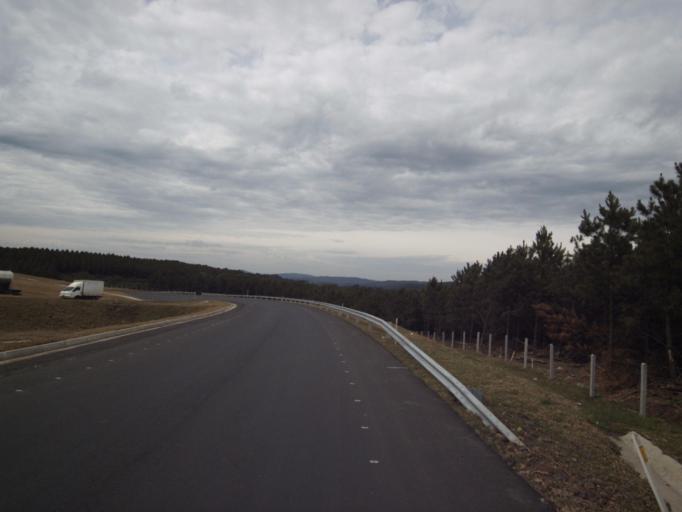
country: BR
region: Santa Catarina
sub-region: Cacador
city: Cacador
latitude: -26.6107
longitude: -51.4818
